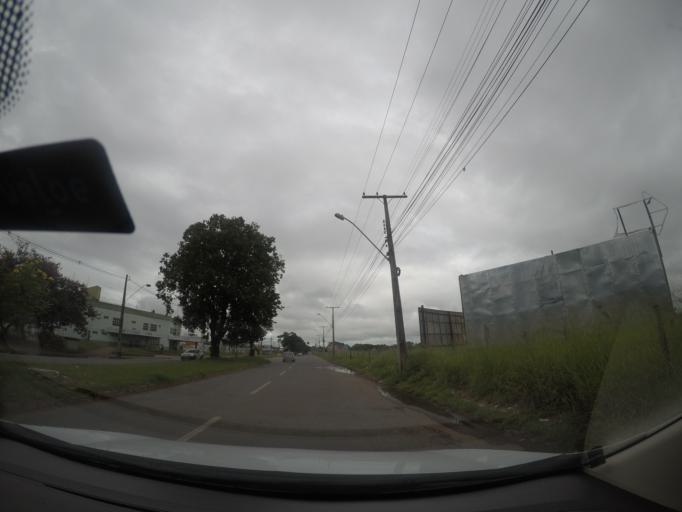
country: BR
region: Goias
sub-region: Goiania
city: Goiania
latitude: -16.7470
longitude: -49.3040
